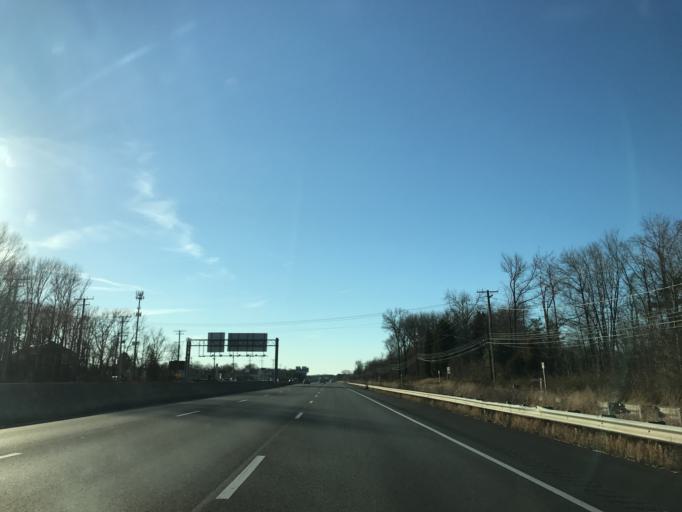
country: US
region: Maryland
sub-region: Anne Arundel County
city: Cape Saint Claire
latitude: 39.0213
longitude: -76.4193
